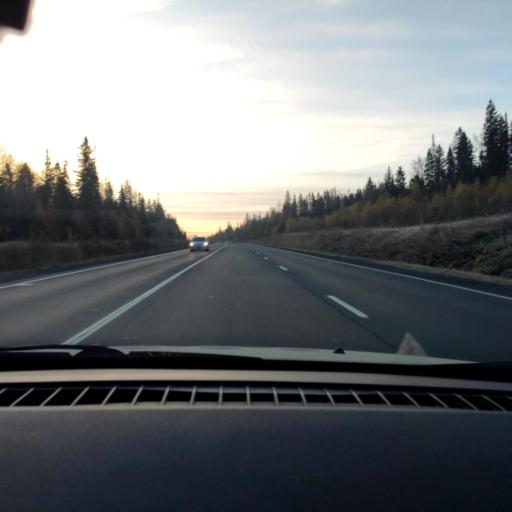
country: RU
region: Perm
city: Novyye Lyady
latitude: 58.0348
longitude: 56.4753
